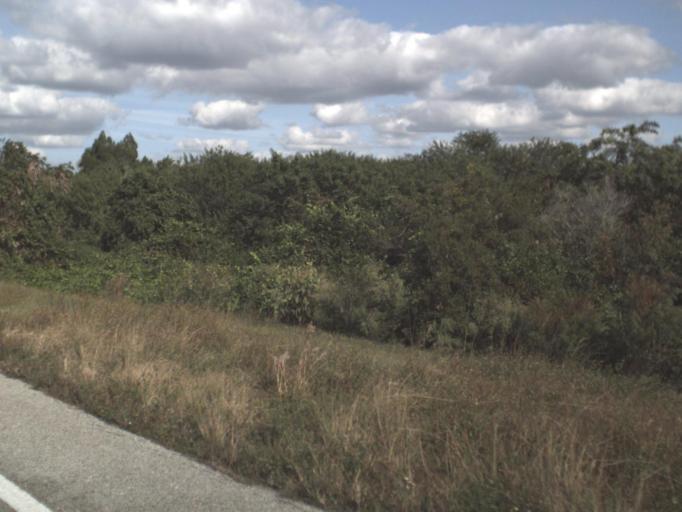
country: US
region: Florida
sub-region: Brevard County
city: Port Saint John
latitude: 28.4932
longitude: -80.8444
